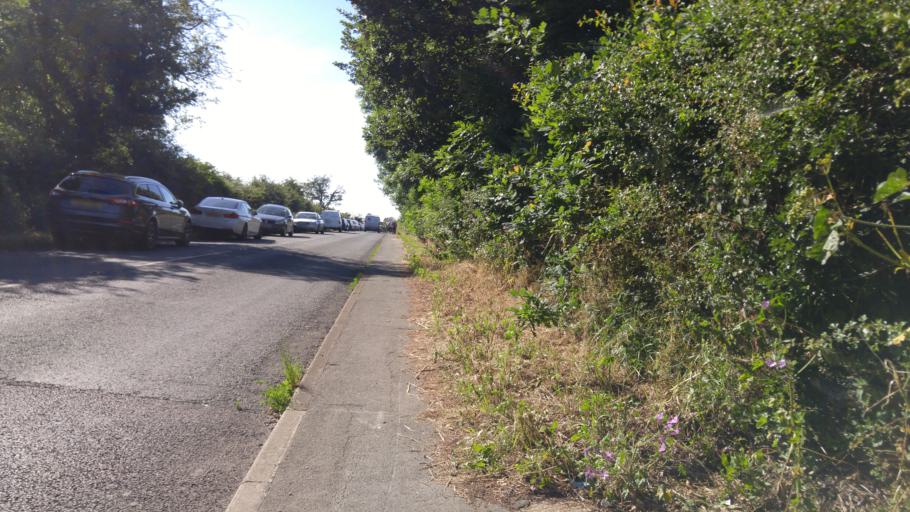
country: GB
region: England
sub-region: Essex
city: Rowhedge
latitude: 51.8586
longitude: 0.9417
